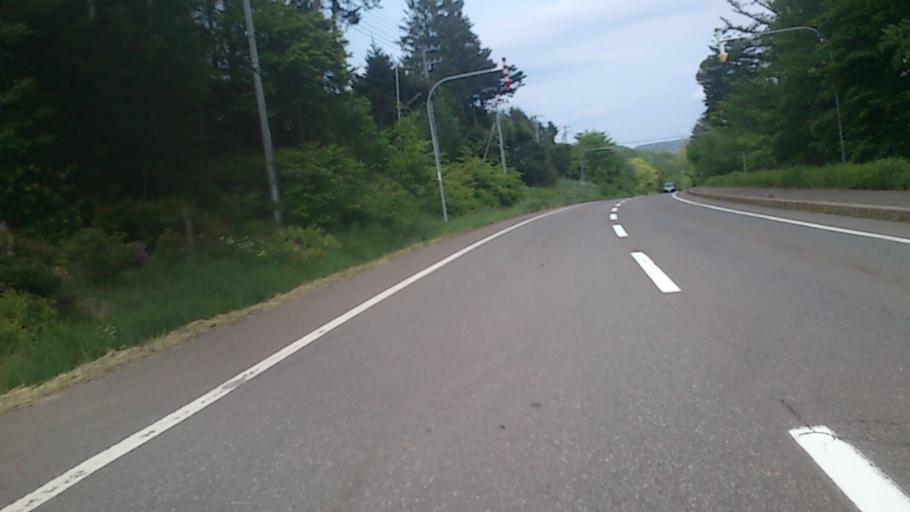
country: JP
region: Hokkaido
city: Otofuke
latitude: 43.2864
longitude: 143.6360
